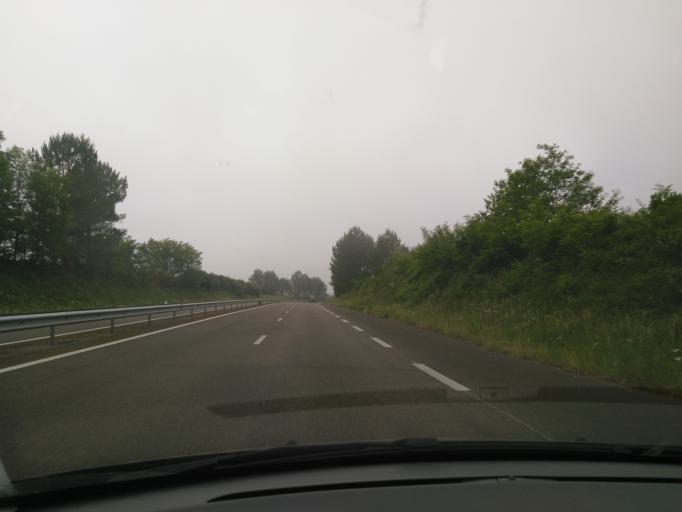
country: FR
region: Aquitaine
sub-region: Departement des Landes
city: Meilhan
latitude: 43.8615
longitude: -0.6936
